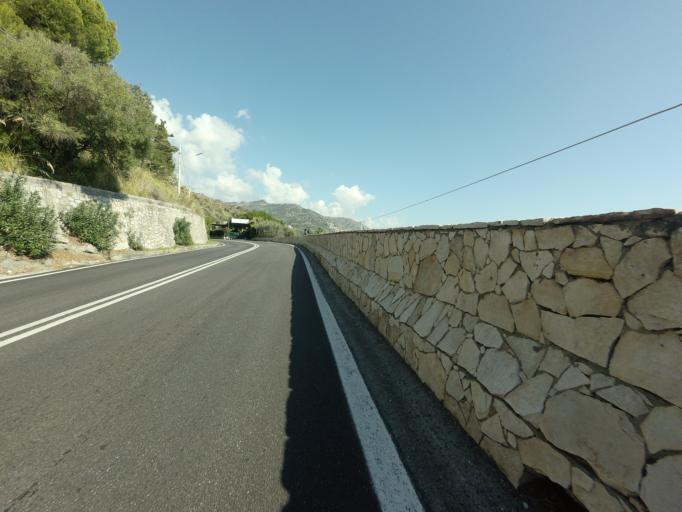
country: IT
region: Sicily
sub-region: Messina
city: Letojanni
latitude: 37.8671
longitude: 15.2982
